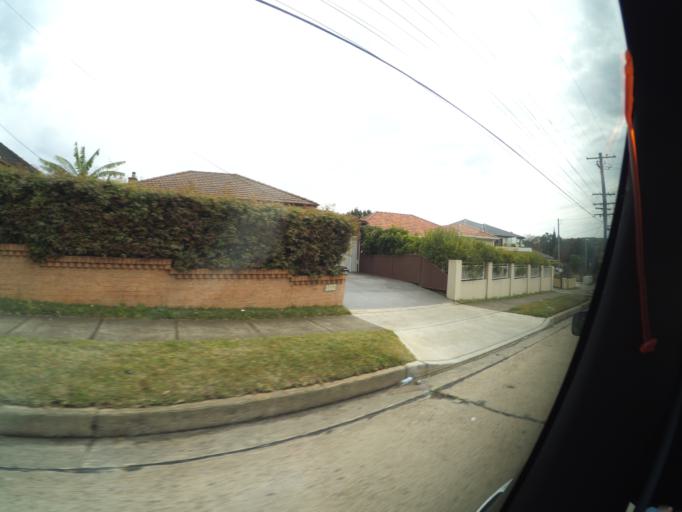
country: AU
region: New South Wales
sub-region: Bankstown
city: Bankstown
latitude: -33.9293
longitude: 151.0298
